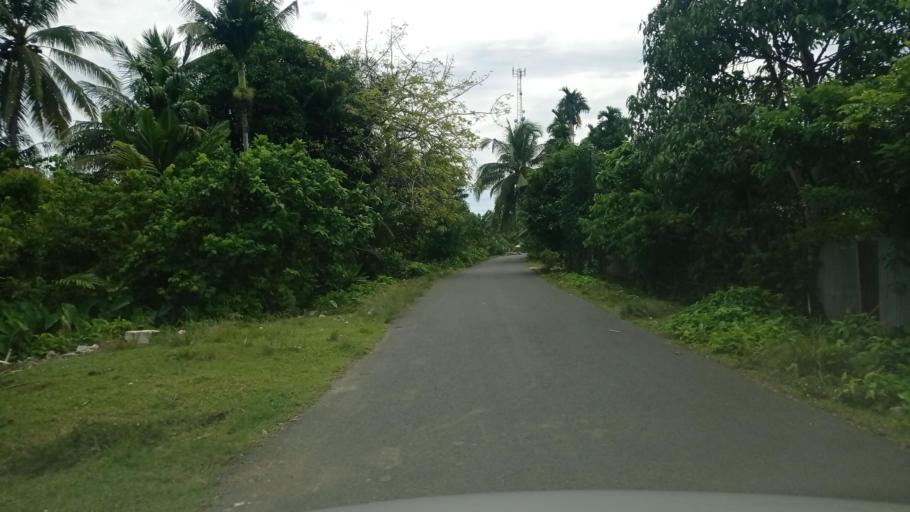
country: ID
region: Bengkulu
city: Ipuh
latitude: -2.5820
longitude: 101.1177
